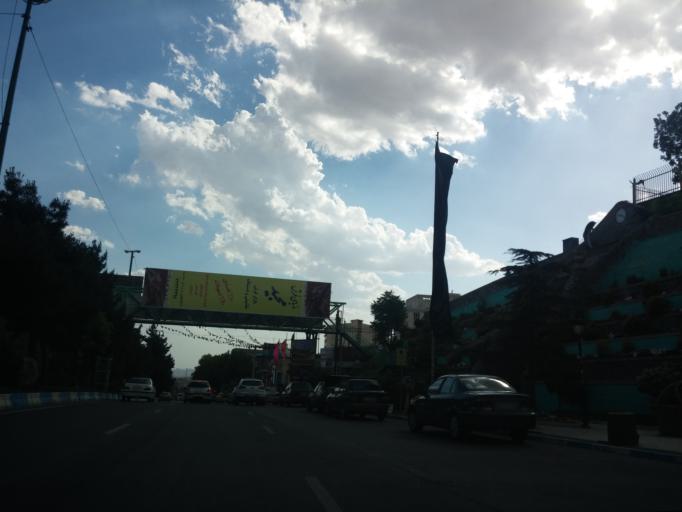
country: IR
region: Tehran
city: Damavand
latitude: 35.7354
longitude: 51.9090
